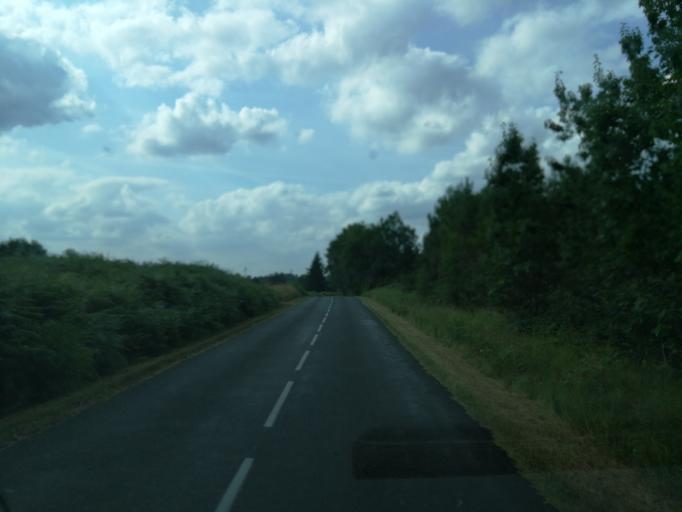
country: FR
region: Aquitaine
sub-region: Departement du Lot-et-Garonne
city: Monsempron-Libos
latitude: 44.5343
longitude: 0.9246
